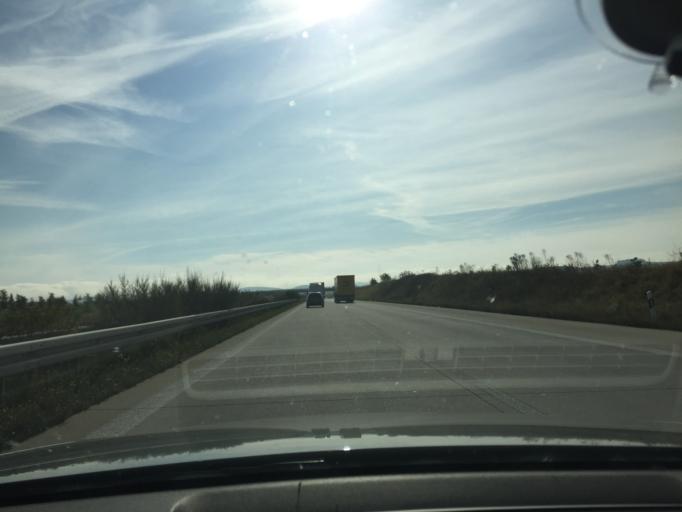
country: DE
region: Saxony
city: Dohma
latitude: 50.9129
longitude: 13.8927
